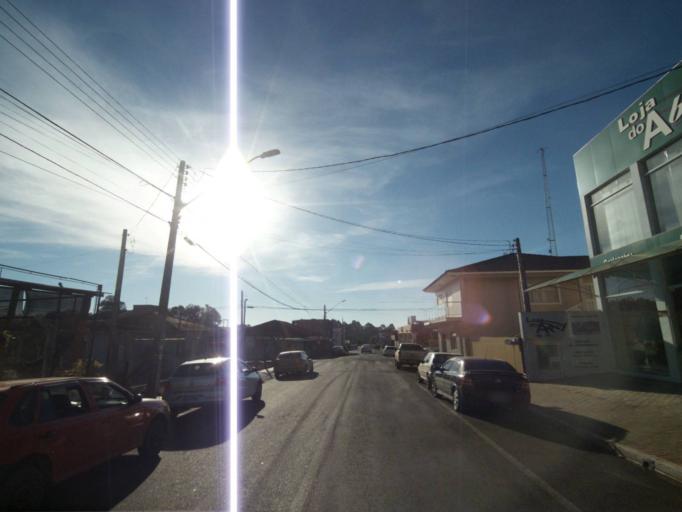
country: BR
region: Parana
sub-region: Tibagi
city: Tibagi
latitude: -24.5122
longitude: -50.4130
